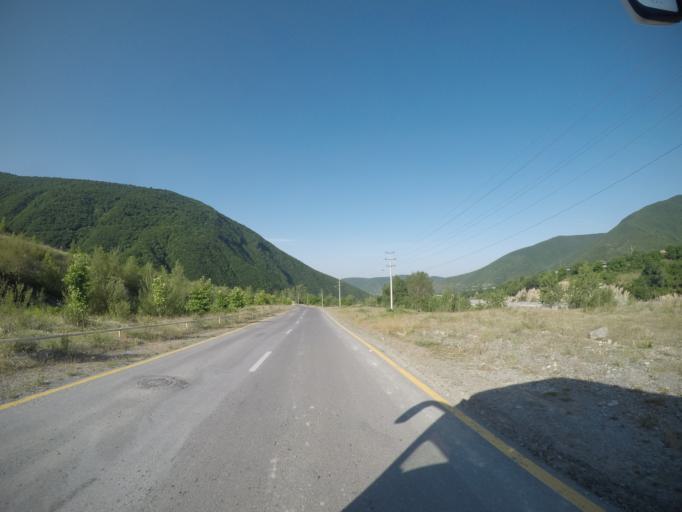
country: AZ
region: Shaki City
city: Sheki
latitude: 41.2503
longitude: 47.2045
